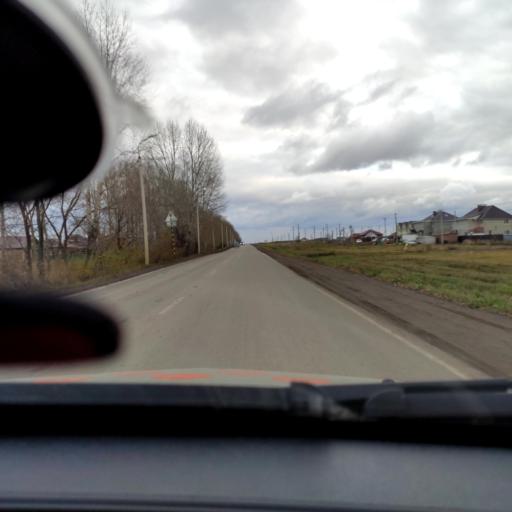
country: RU
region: Bashkortostan
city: Kabakovo
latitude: 54.6158
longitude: 56.1362
